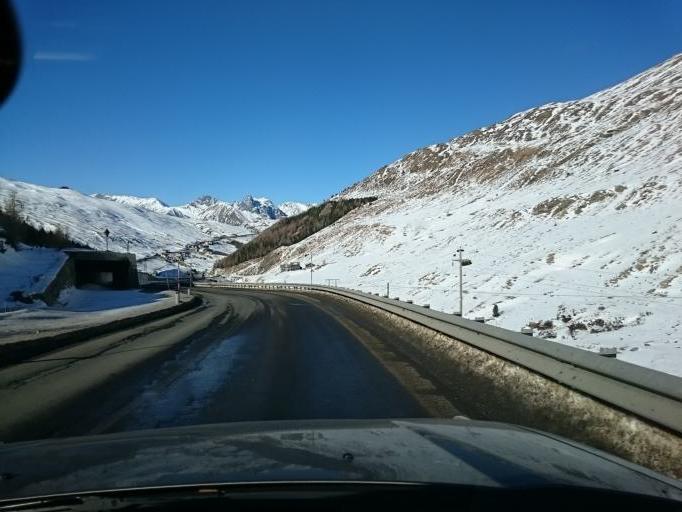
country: IT
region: Lombardy
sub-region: Provincia di Sondrio
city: Livigno
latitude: 46.5123
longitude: 10.1949
